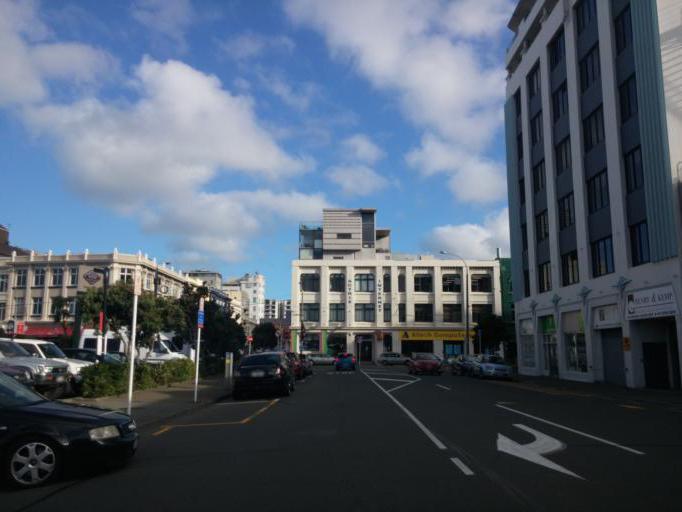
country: NZ
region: Wellington
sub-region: Wellington City
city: Wellington
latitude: -41.2921
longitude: 174.7835
